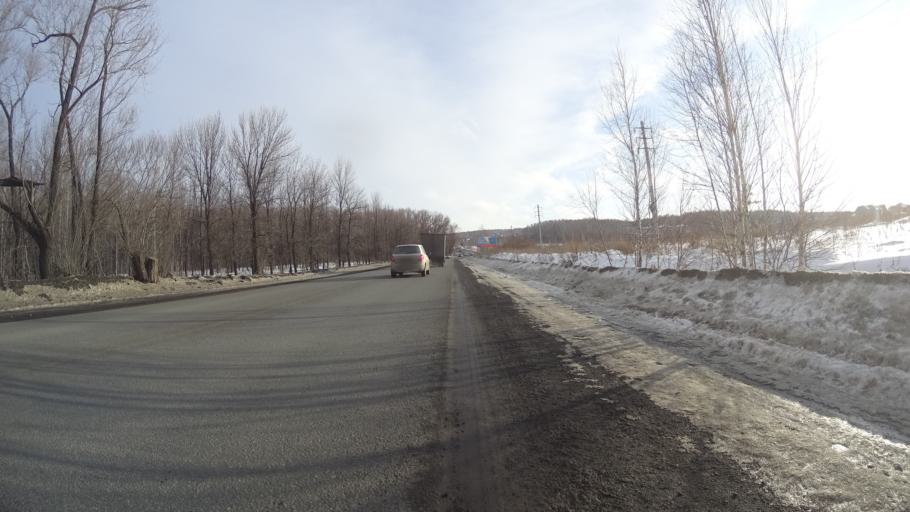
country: RU
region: Chelyabinsk
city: Sargazy
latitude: 55.1394
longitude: 61.2823
